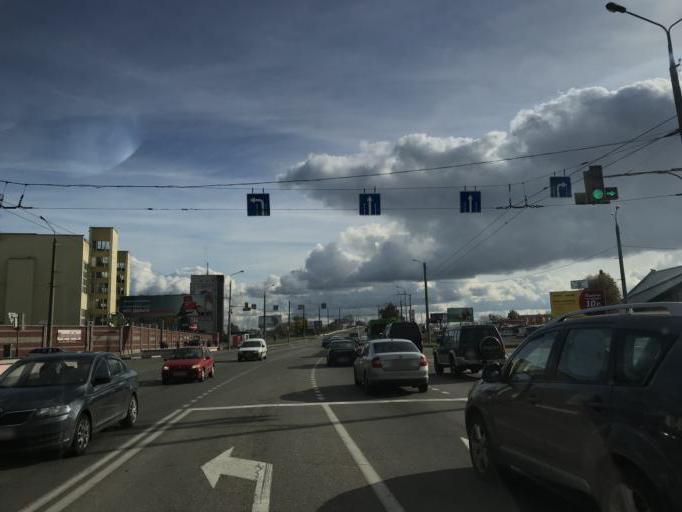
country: BY
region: Gomel
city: Gomel
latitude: 52.4477
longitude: 30.9701
